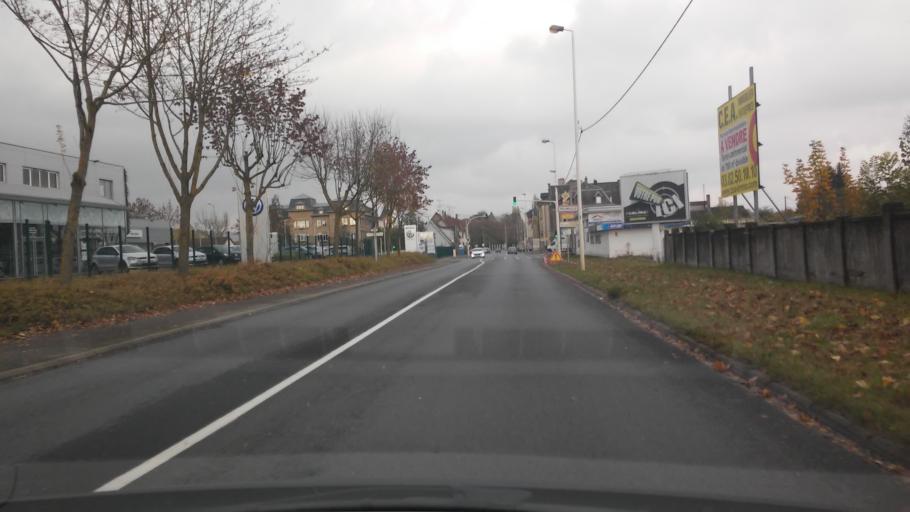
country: FR
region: Lorraine
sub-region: Departement de la Moselle
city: Terville
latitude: 49.3414
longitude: 6.1604
